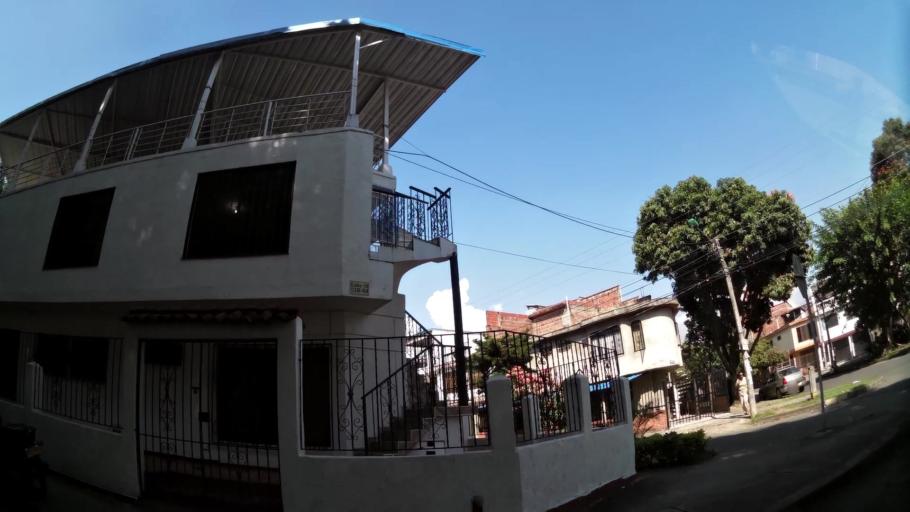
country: CO
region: Valle del Cauca
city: Cali
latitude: 3.4039
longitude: -76.5256
